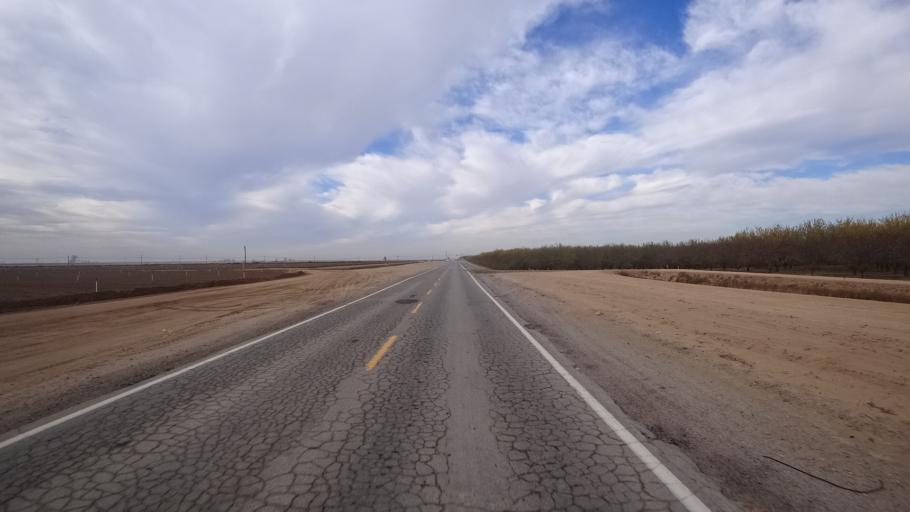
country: US
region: California
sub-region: Kern County
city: Rosedale
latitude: 35.4198
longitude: -119.1670
